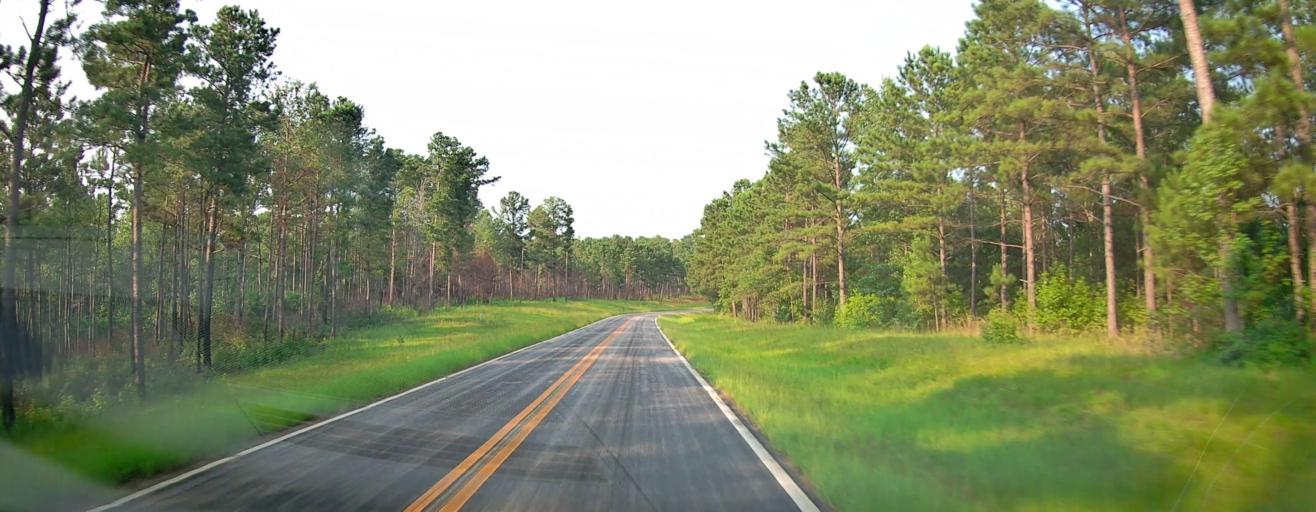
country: US
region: Georgia
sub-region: Jones County
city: Gray
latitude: 33.1126
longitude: -83.6558
